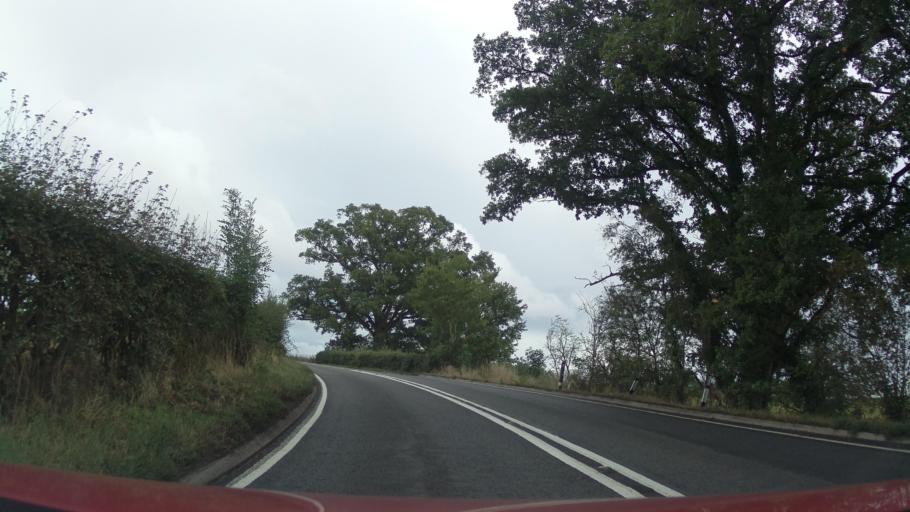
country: GB
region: England
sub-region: Worcestershire
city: Stourport-on-Severn
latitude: 52.3398
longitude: -2.1928
